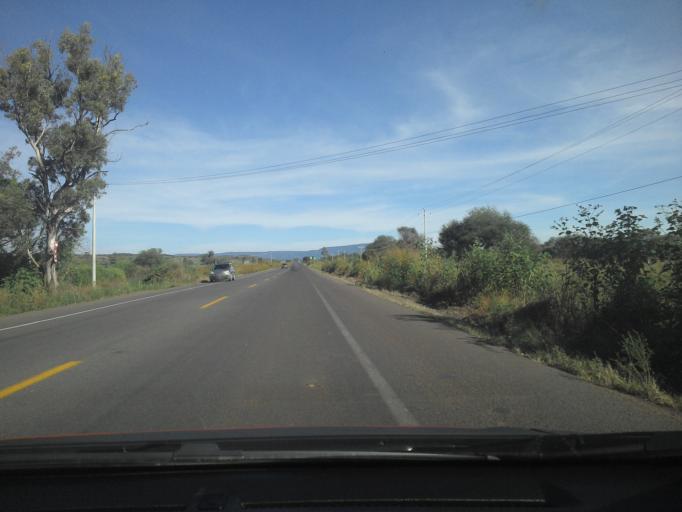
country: MX
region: Jalisco
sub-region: Teuchitlan
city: La Estanzuela
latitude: 20.6721
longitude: -103.8181
